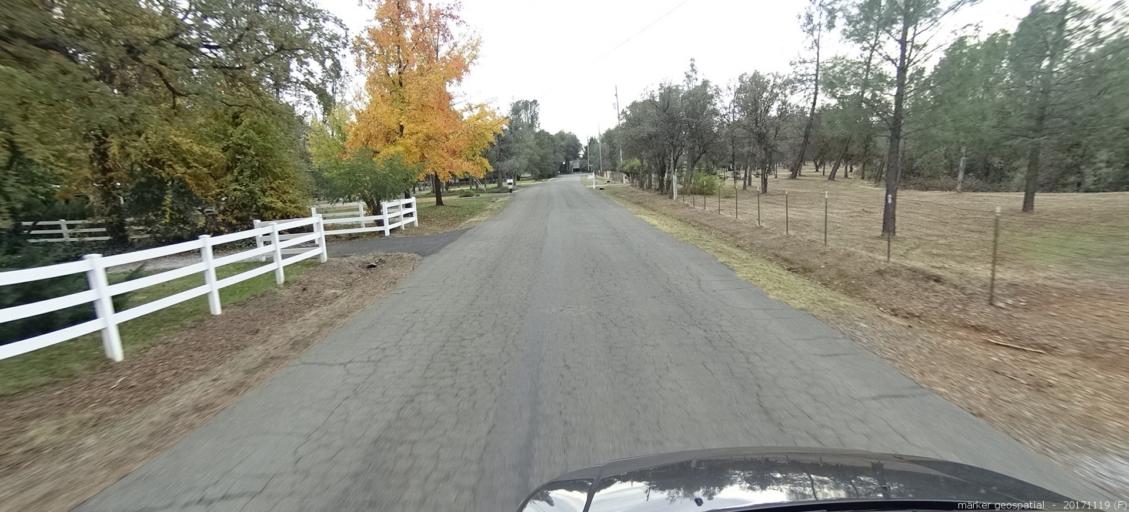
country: US
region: California
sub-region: Shasta County
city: Shasta
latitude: 40.4798
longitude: -122.4641
